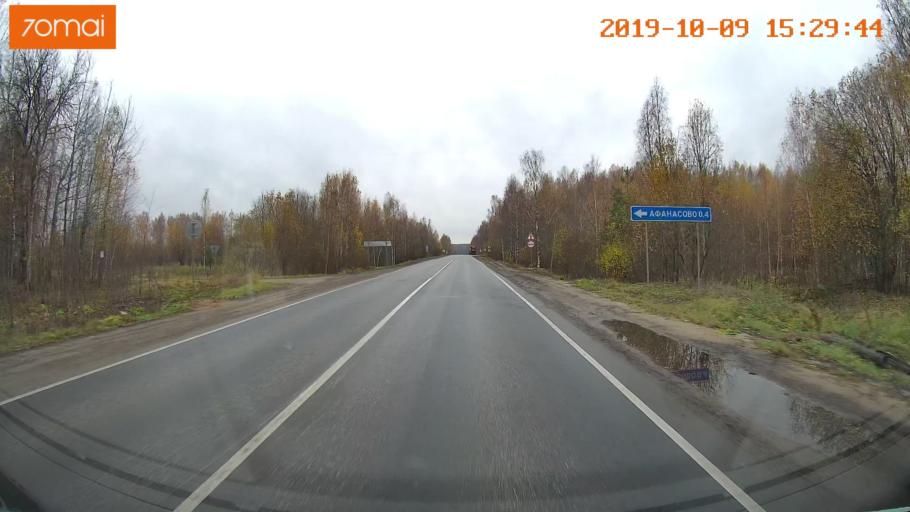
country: RU
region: Kostroma
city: Susanino
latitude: 57.9880
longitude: 41.3377
